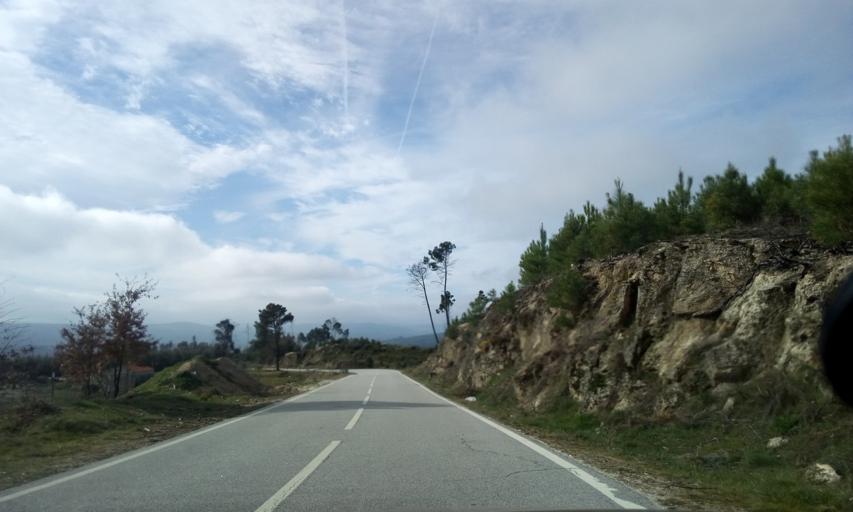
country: PT
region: Guarda
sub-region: Aguiar da Beira
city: Aguiar da Beira
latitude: 40.7505
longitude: -7.5491
